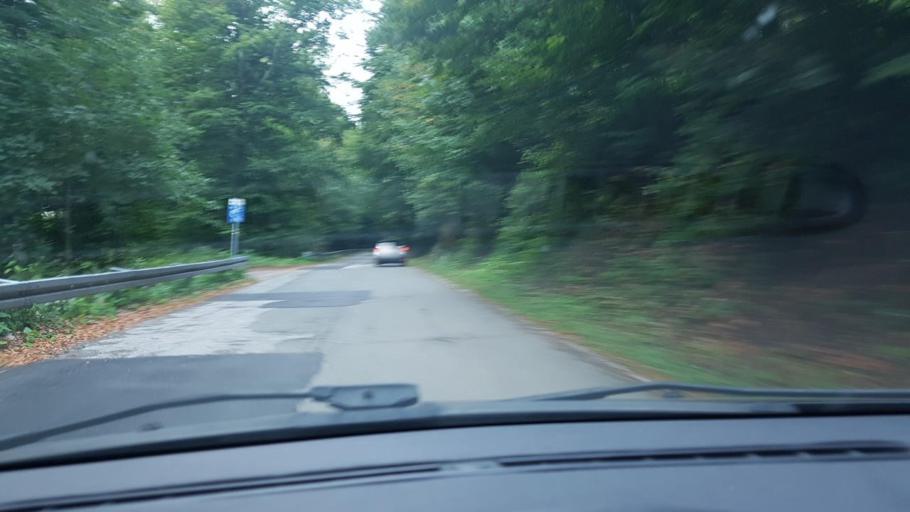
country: HR
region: Grad Zagreb
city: Kasina
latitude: 45.8978
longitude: 15.9461
